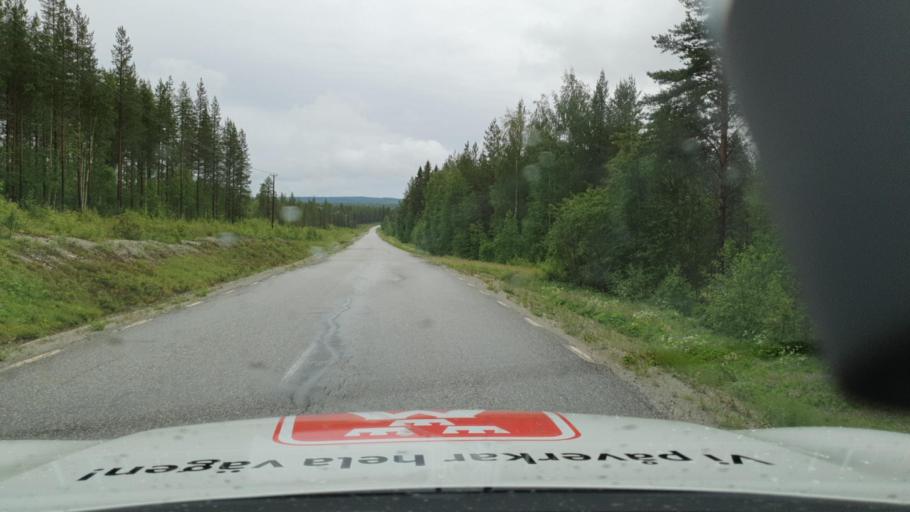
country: SE
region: Vaesterbotten
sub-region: Asele Kommun
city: Asele
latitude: 63.9954
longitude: 17.1711
